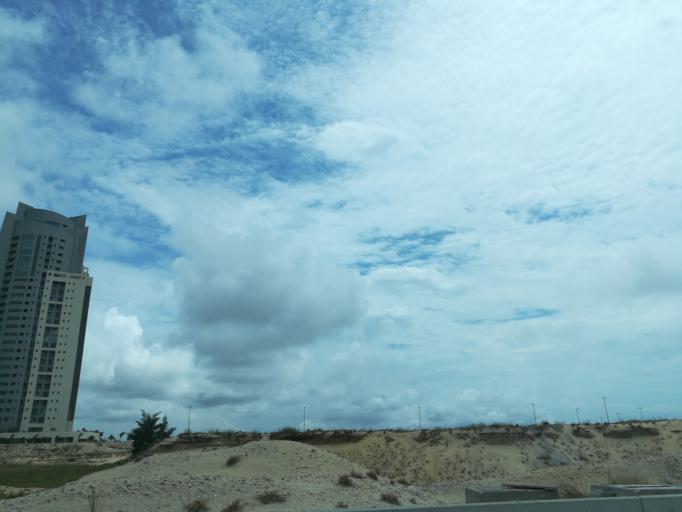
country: NG
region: Lagos
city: Lagos
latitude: 6.4065
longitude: 3.4092
